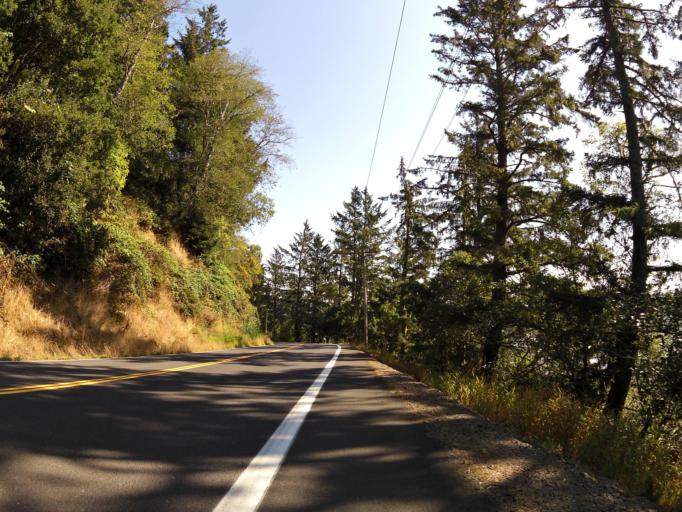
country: US
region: Oregon
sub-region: Tillamook County
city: Pacific City
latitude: 45.1812
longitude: -123.9440
